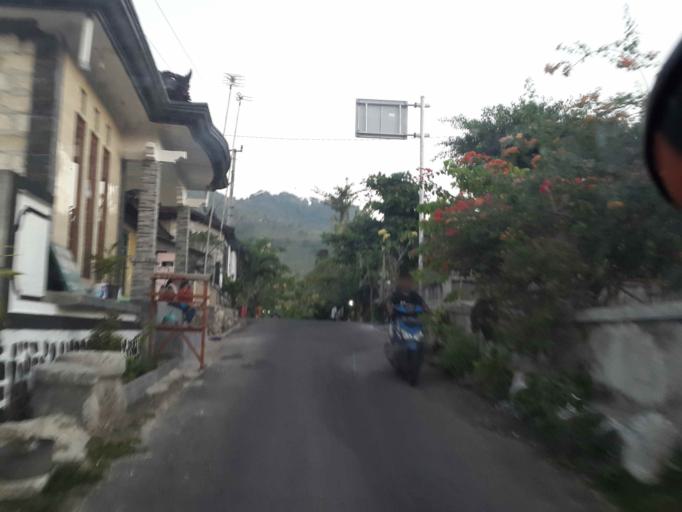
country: ID
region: Bali
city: Klumbu
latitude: -8.7181
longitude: 115.5230
